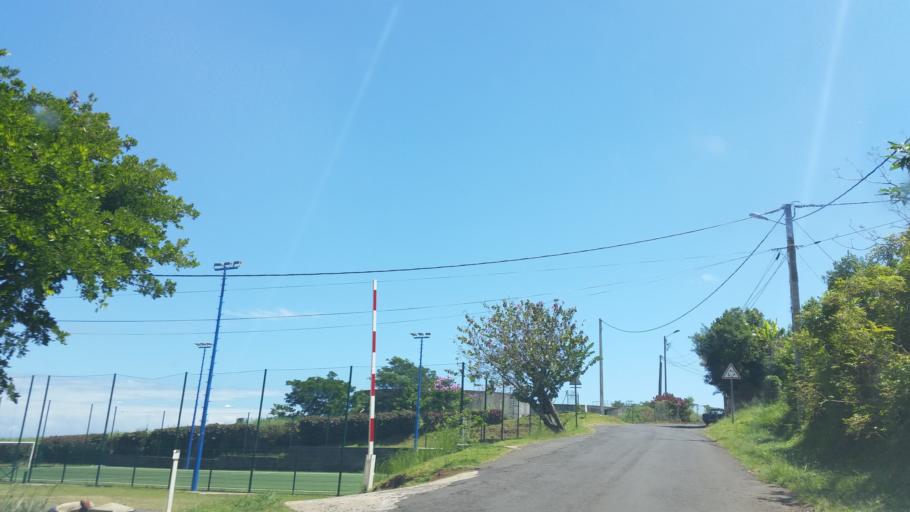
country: RE
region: Reunion
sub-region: Reunion
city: Sainte-Marie
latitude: -20.9311
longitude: 55.5303
